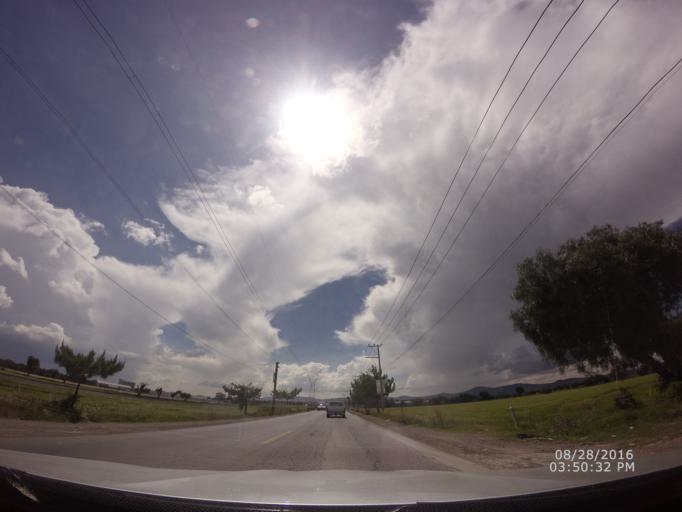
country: MX
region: Hidalgo
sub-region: Mineral de la Reforma
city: Rinconada de los Angeles
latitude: 20.0371
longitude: -98.7345
